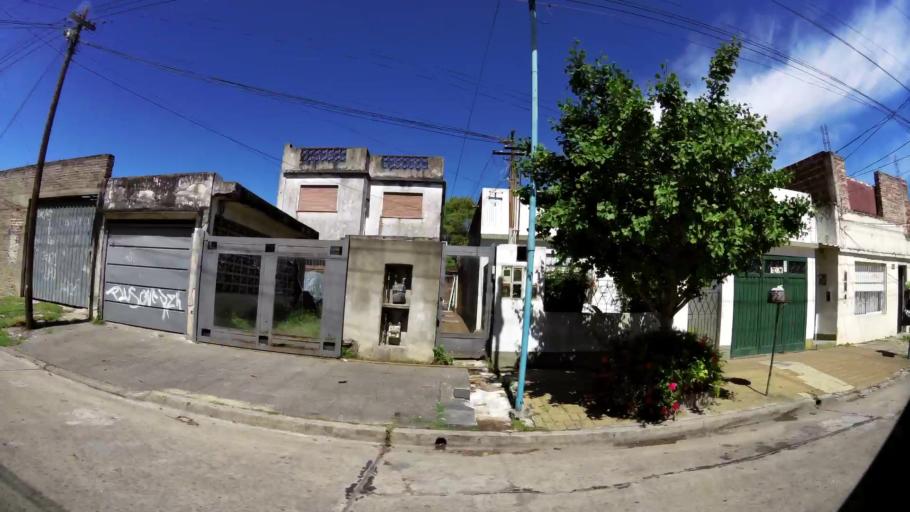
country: AR
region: Buenos Aires
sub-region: Partido de Quilmes
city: Quilmes
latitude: -34.7095
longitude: -58.2638
